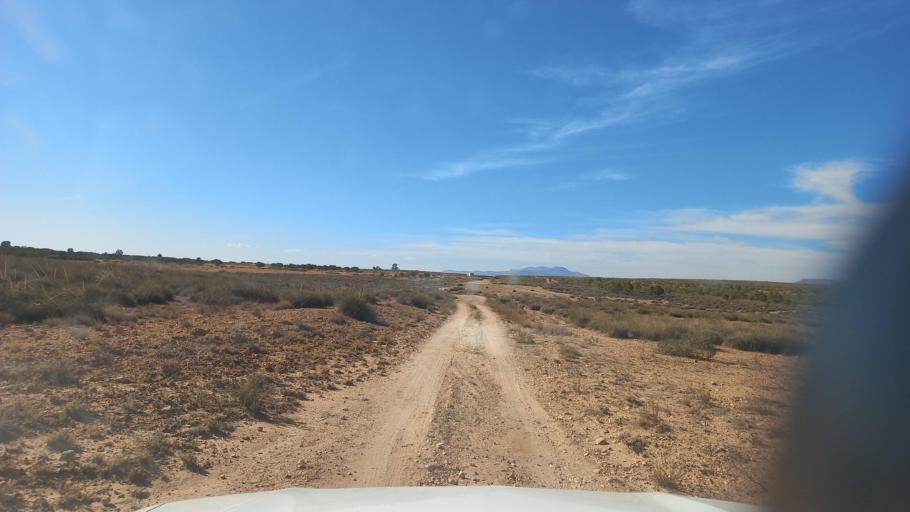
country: TN
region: Al Qasrayn
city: Kasserine
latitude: 35.2151
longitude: 8.9830
